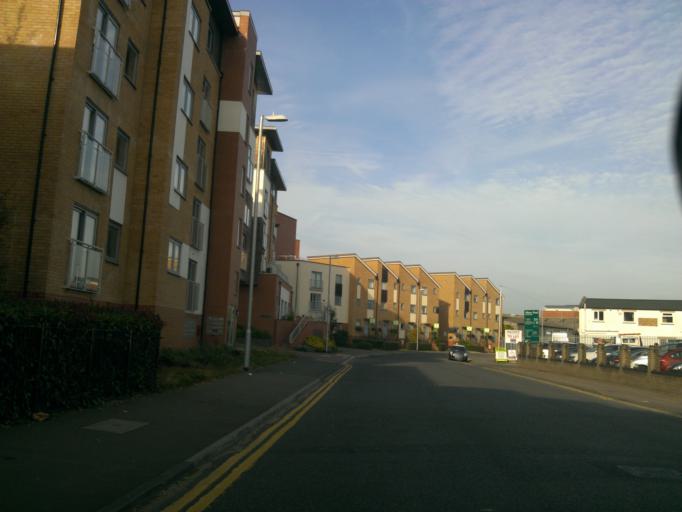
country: GB
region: England
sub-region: Essex
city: Colchester
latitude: 51.8818
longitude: 0.9287
